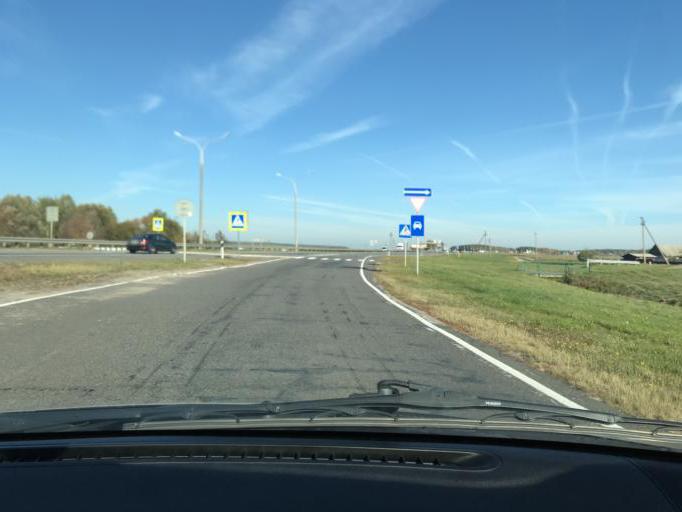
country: BY
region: Brest
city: Ivatsevichy
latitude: 52.6994
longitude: 25.3654
